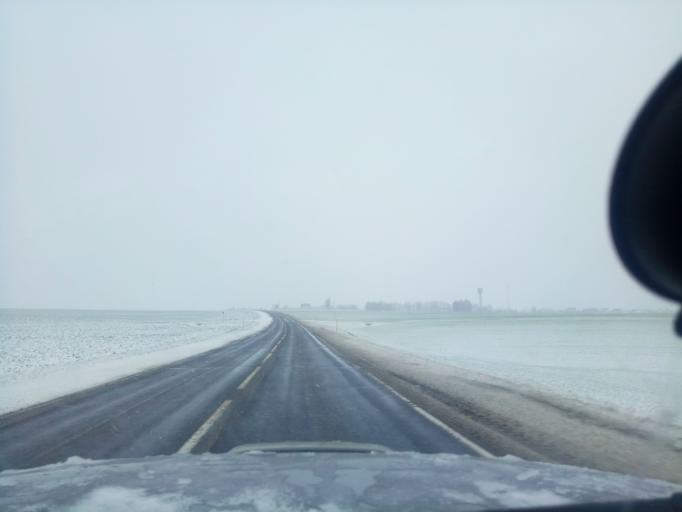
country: BY
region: Minsk
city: Haradzyeya
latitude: 53.3252
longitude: 26.5530
